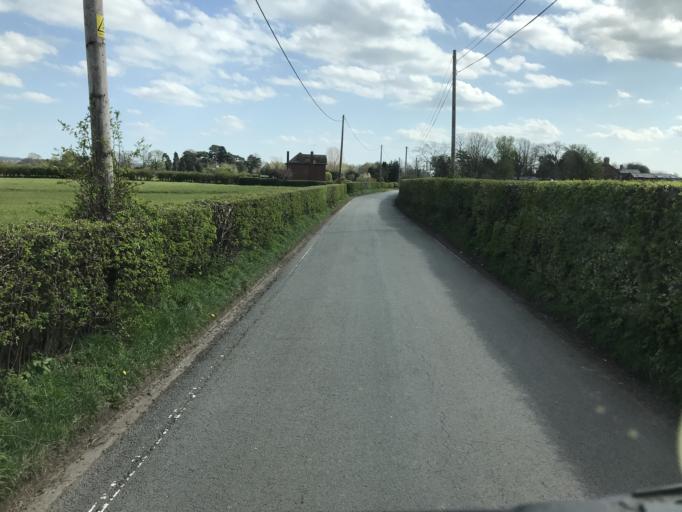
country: GB
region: England
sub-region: Cheshire West and Chester
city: Tarvin
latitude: 53.2063
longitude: -2.7655
